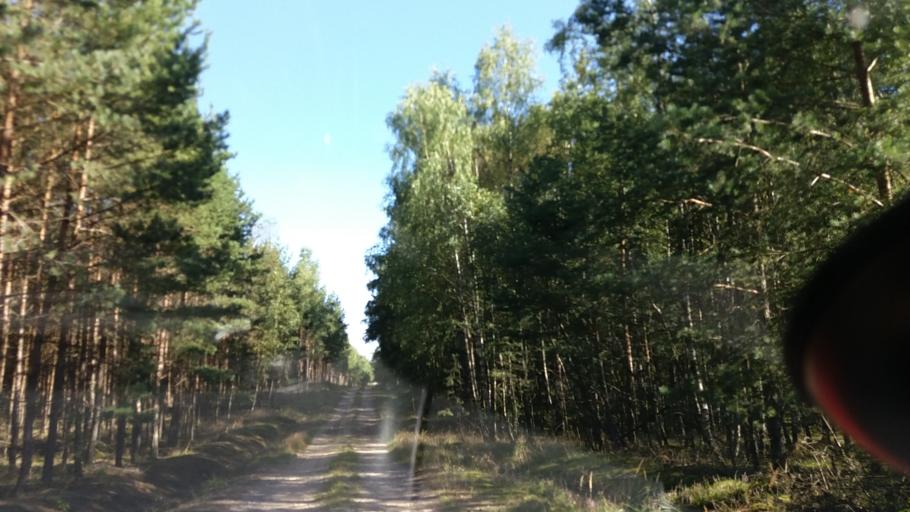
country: PL
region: West Pomeranian Voivodeship
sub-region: Powiat szczecinecki
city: Borne Sulinowo
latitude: 53.5732
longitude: 16.4868
